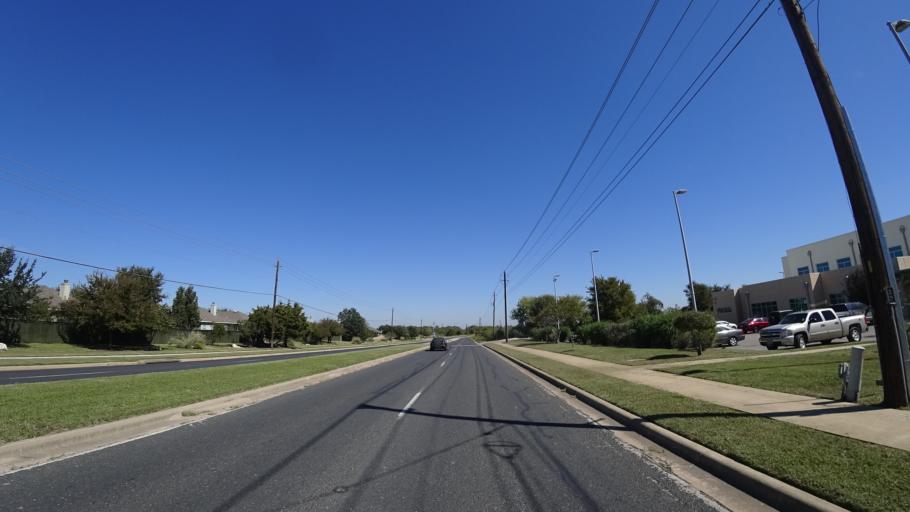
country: US
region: Texas
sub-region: Travis County
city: Austin
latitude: 30.1954
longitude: -97.6944
